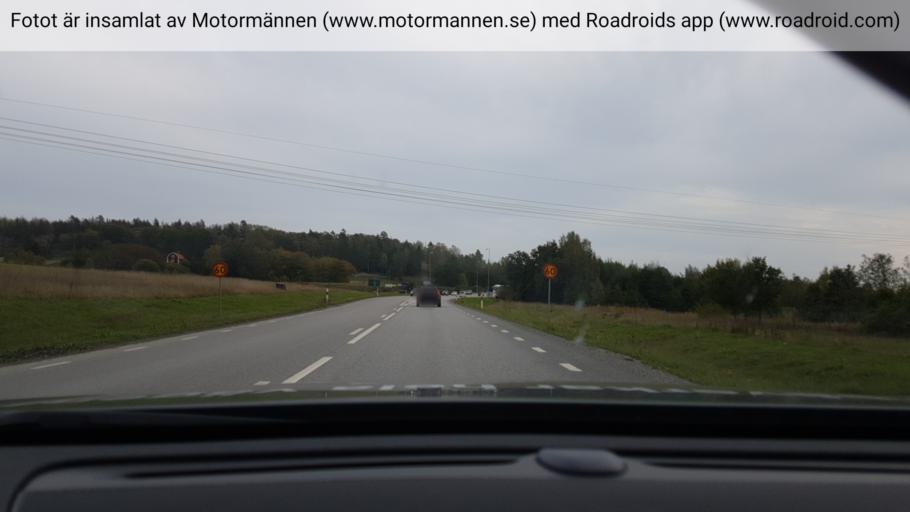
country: SE
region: Stockholm
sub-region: Nynashamns Kommun
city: Nynashamn
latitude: 58.9301
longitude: 17.9295
